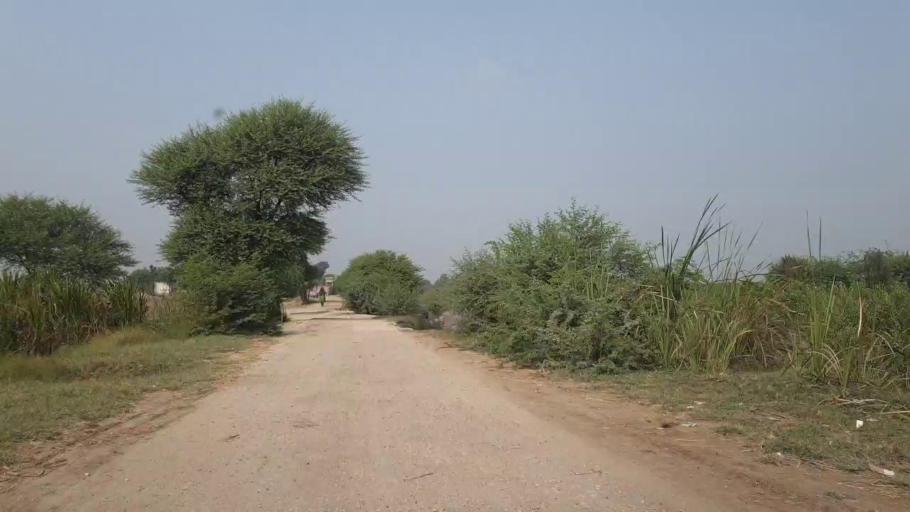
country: PK
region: Sindh
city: Matli
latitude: 25.0259
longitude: 68.5970
